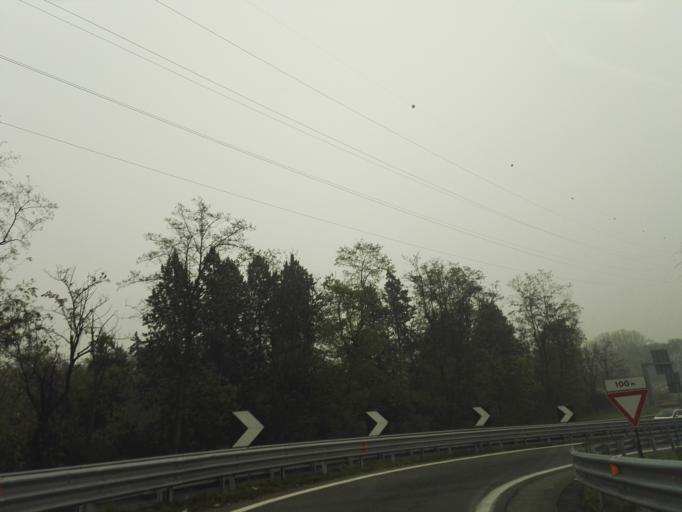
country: IT
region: Lombardy
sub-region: Citta metropolitana di Milano
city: Figino
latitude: 45.4898
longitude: 9.0674
